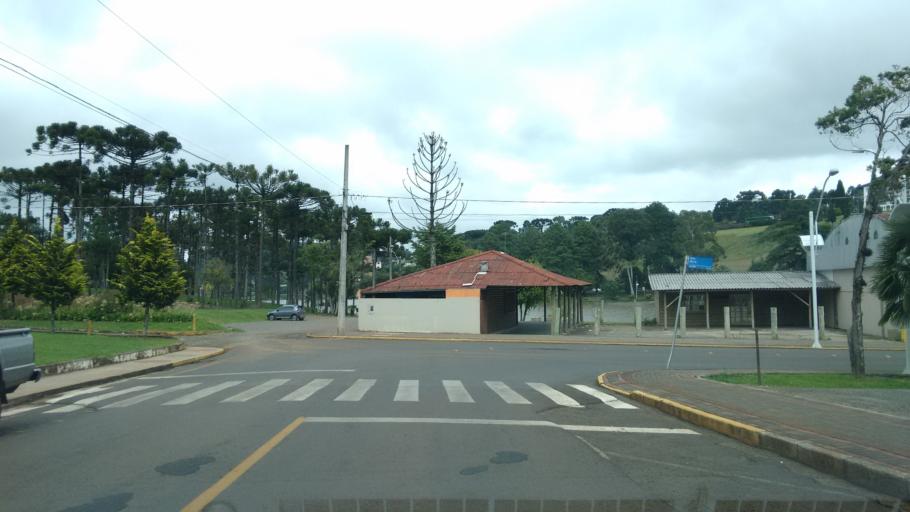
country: BR
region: Santa Catarina
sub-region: Videira
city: Videira
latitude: -27.0267
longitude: -50.9244
